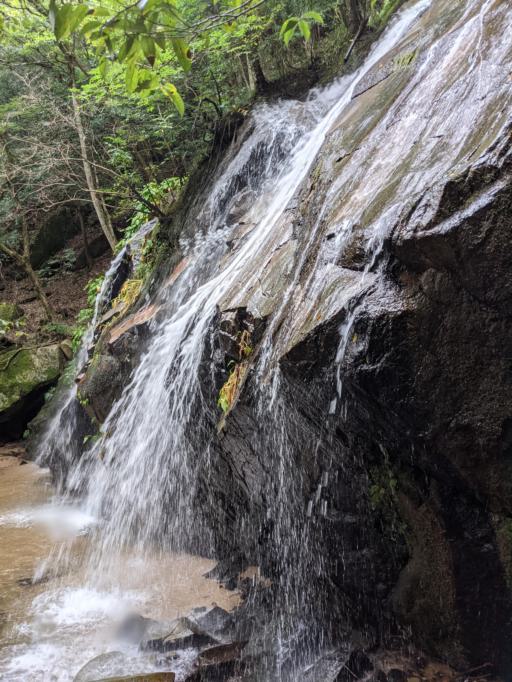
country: JP
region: Kyoto
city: Miyazu
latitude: 35.5294
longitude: 135.1829
